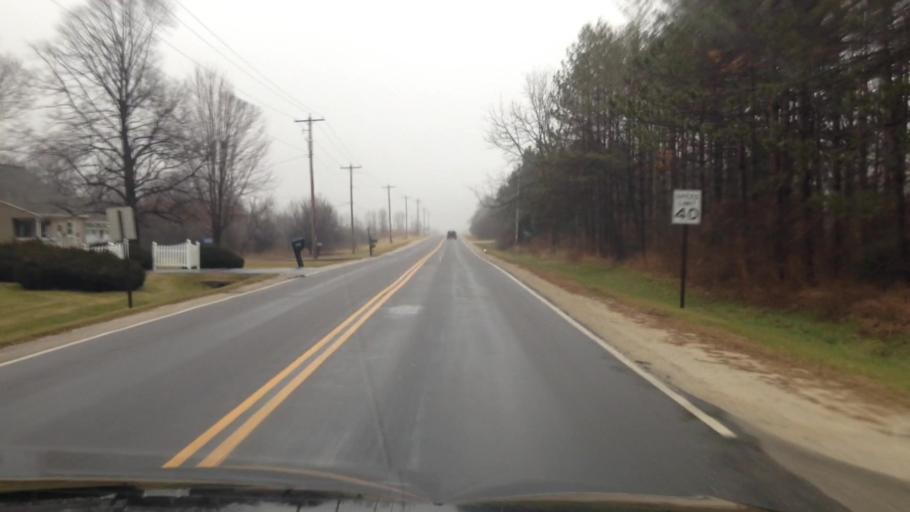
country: US
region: Wisconsin
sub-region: Washington County
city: Richfield
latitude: 43.2358
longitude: -88.1590
